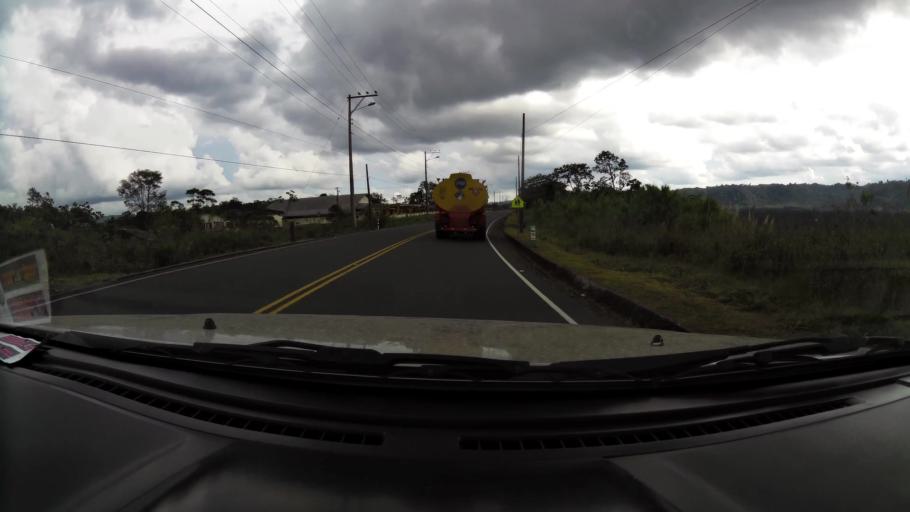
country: EC
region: Pastaza
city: Puyo
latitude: -1.4522
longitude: -78.1231
